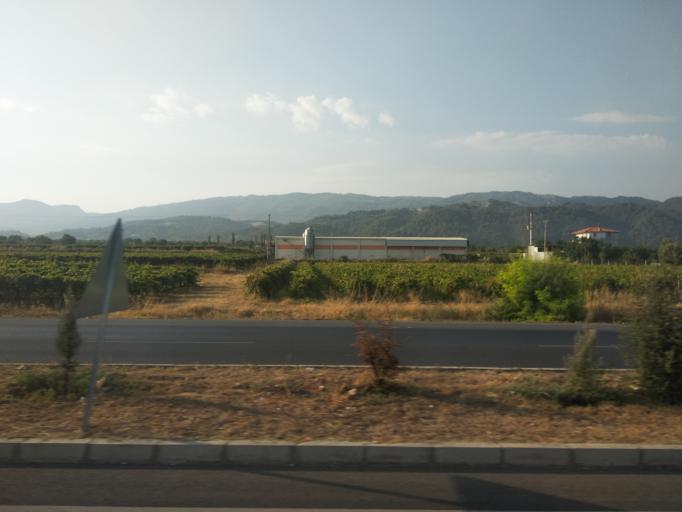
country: TR
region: Manisa
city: Ahmetli
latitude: 38.5052
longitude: 27.8835
